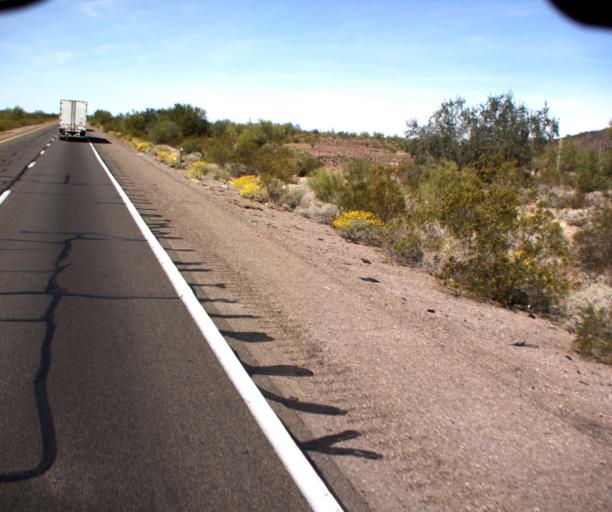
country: US
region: Arizona
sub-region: La Paz County
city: Quartzsite
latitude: 33.6501
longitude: -113.9116
